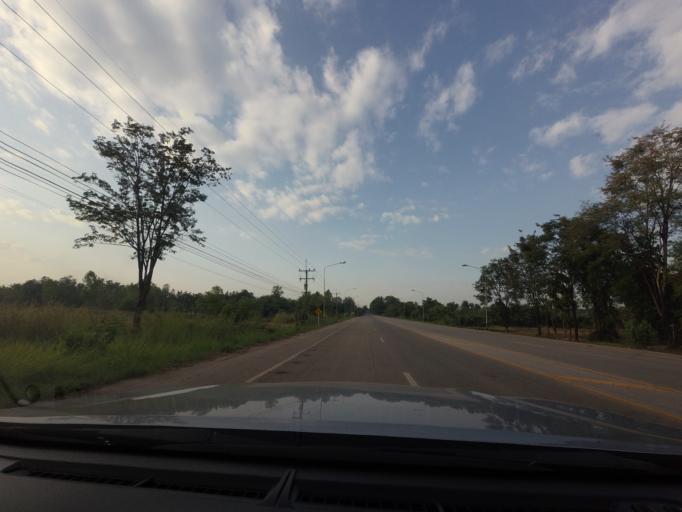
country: TH
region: Phitsanulok
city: Noen Maprang
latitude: 16.5865
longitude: 100.6280
